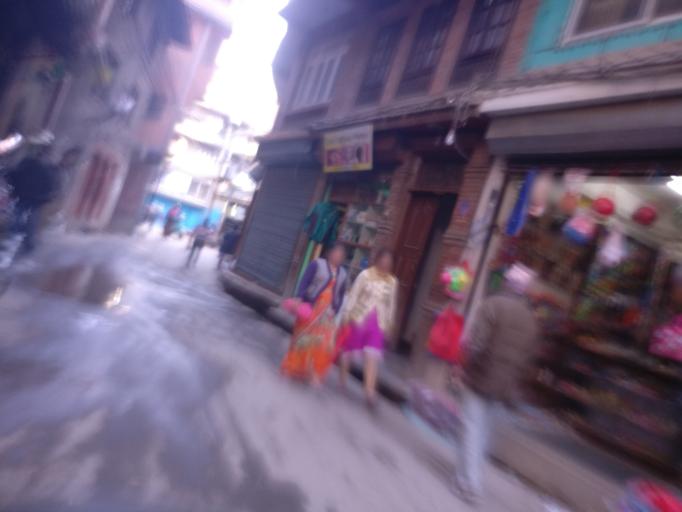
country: NP
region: Central Region
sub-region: Bagmati Zone
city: Kathmandu
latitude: 27.6986
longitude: 85.3070
